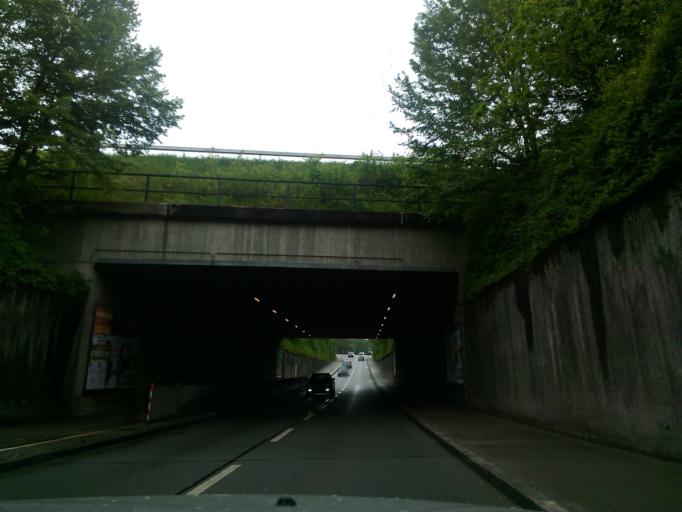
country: DE
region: Bavaria
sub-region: Upper Bavaria
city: Haar
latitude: 48.1214
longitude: 11.6861
